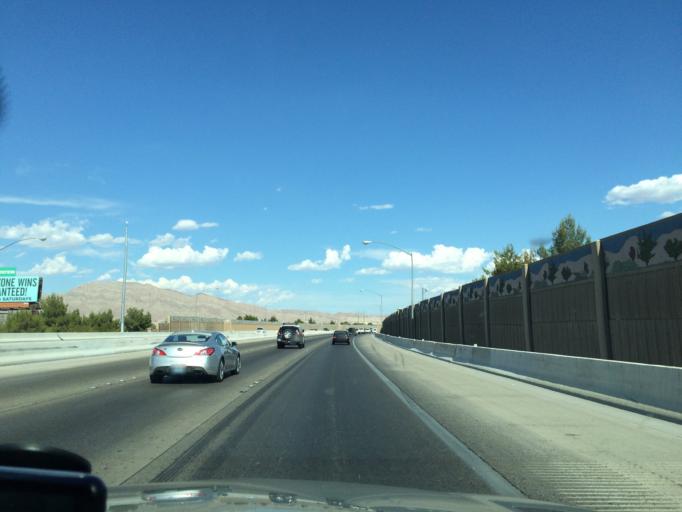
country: US
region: Nevada
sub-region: Clark County
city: North Las Vegas
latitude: 36.1672
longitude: -115.1006
